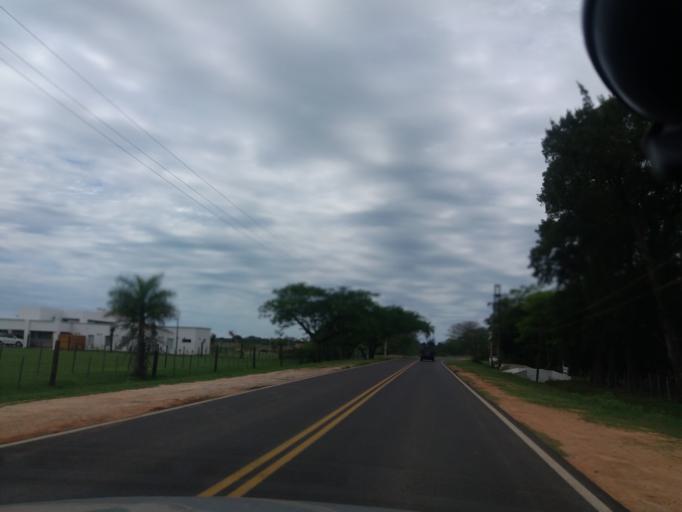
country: AR
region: Corrientes
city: Corrientes
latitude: -27.4563
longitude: -58.7155
